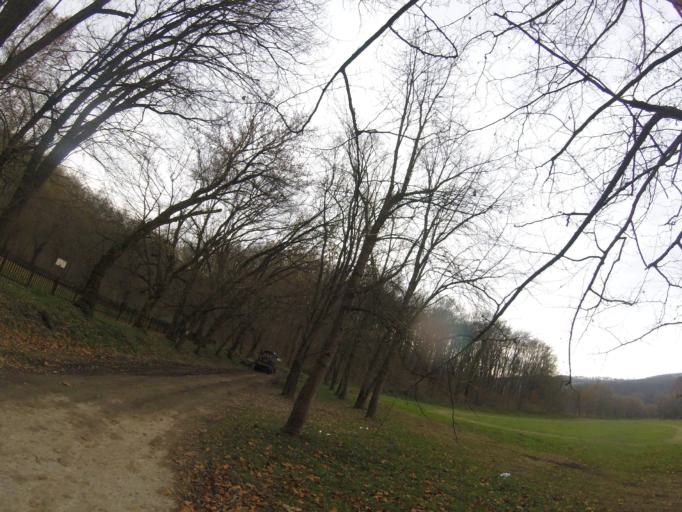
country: HU
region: Tolna
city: Szentgalpuszta
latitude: 46.3420
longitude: 18.6268
